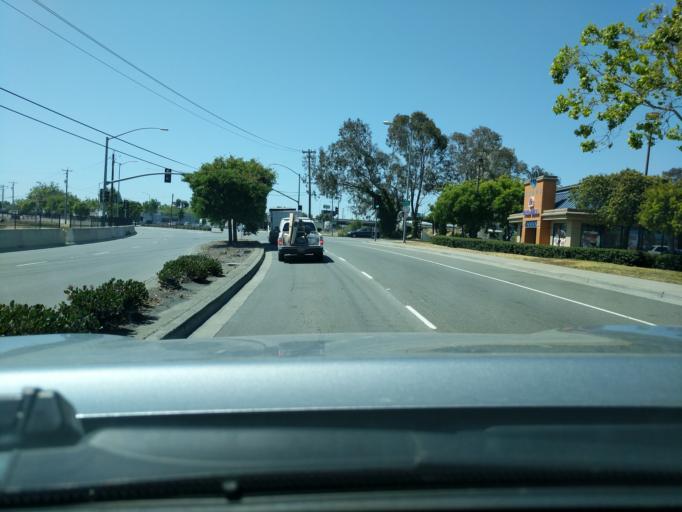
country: US
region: California
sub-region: Alameda County
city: Union City
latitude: 37.6115
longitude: -122.0671
